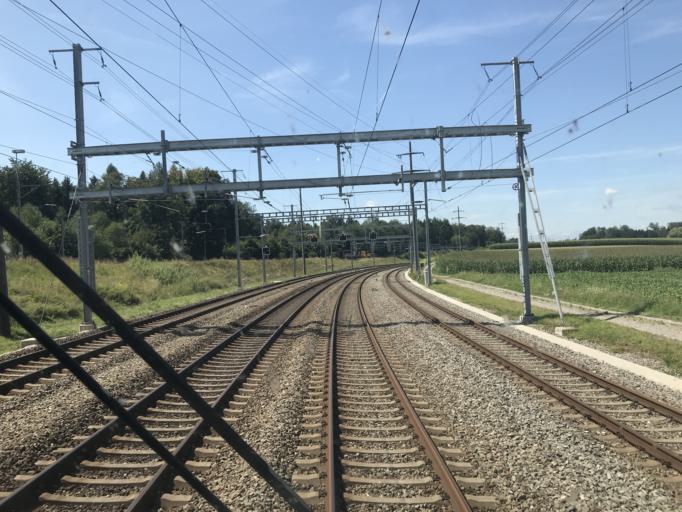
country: CH
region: Zurich
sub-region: Bezirk Pfaeffikon
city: Tagelswangen
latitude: 47.4208
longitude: 8.6796
